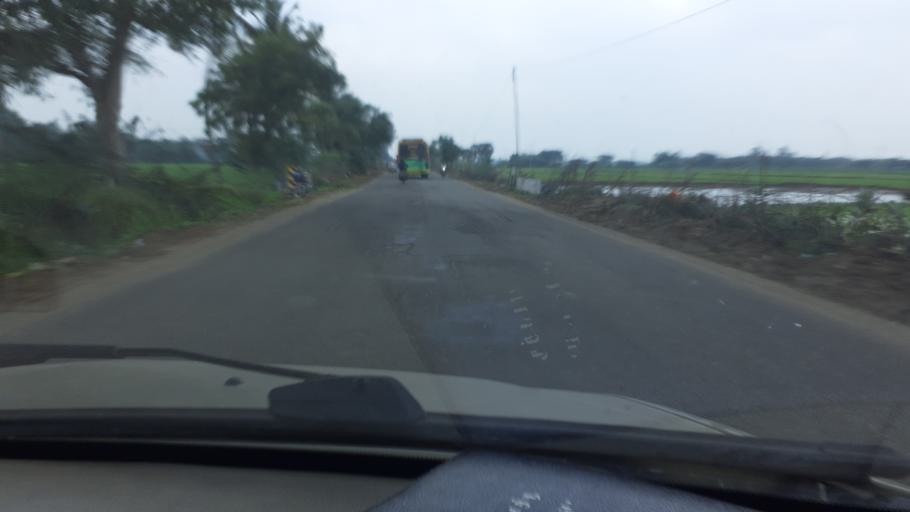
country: IN
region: Tamil Nadu
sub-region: Tirunelveli Kattabo
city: Viravanallur
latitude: 8.7243
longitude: 77.5410
